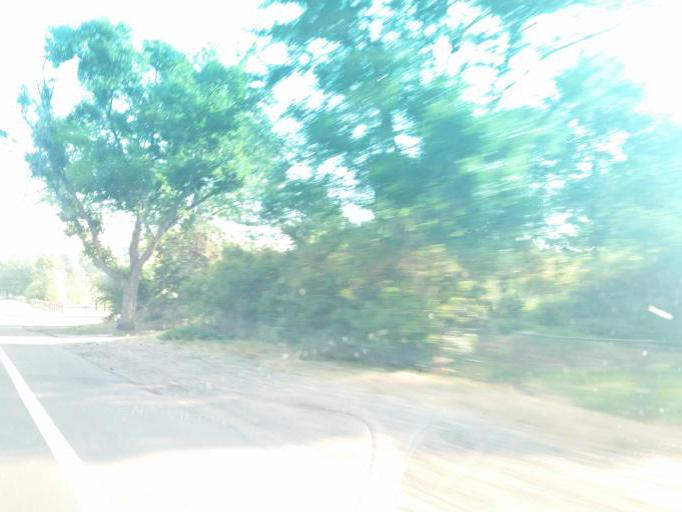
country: US
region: Colorado
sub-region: Larimer County
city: Fort Collins
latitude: 40.5647
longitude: -105.1151
